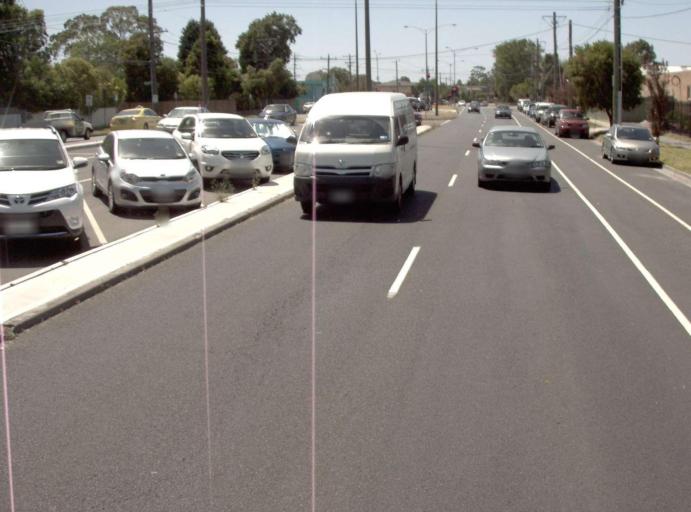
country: AU
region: Victoria
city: Murrumbeena
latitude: -37.9084
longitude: 145.0616
